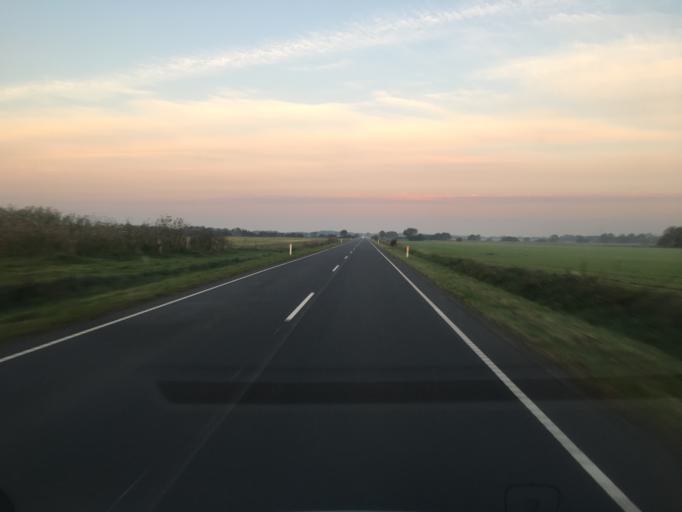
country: DE
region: Schleswig-Holstein
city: Bramstedtlund
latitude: 54.9721
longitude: 9.0778
